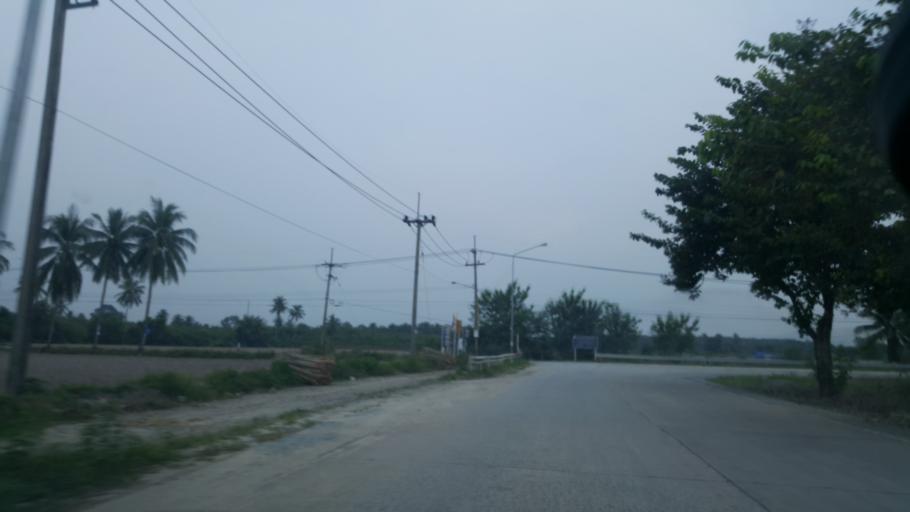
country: TH
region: Chon Buri
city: Si Racha
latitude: 13.2338
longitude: 101.0140
